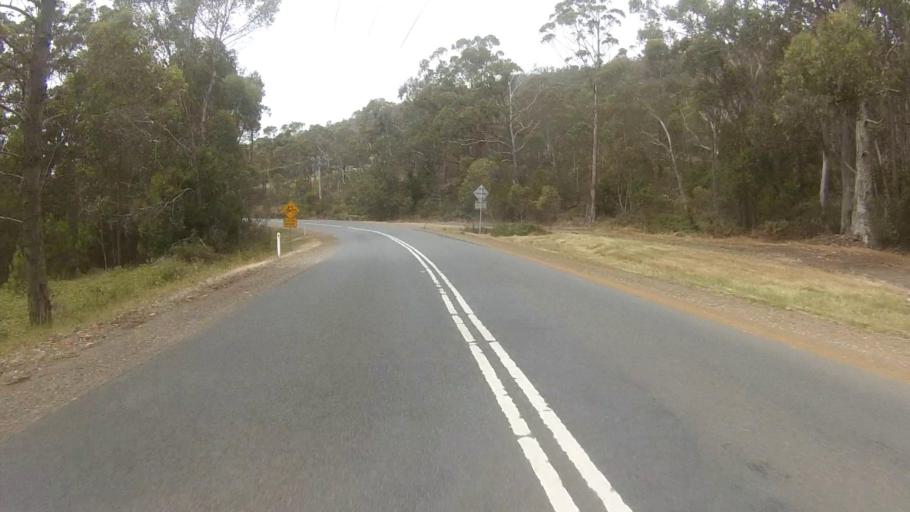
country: AU
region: Tasmania
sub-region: Kingborough
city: Margate
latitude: -42.9997
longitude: 147.2303
